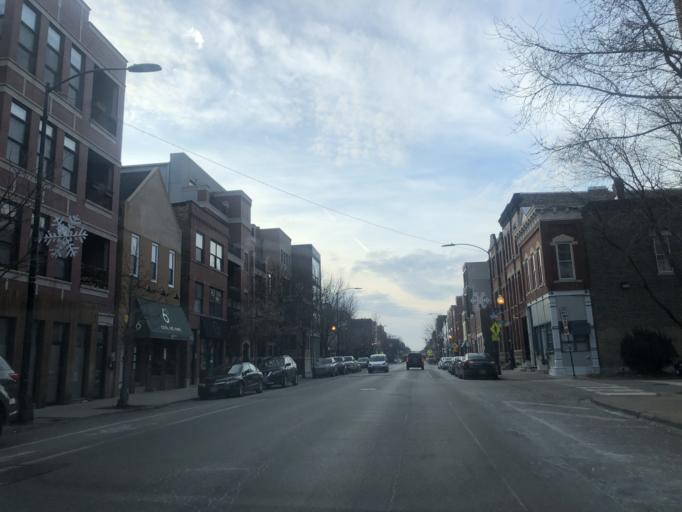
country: US
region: Illinois
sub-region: Cook County
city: Chicago
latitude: 41.9173
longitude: -87.6777
